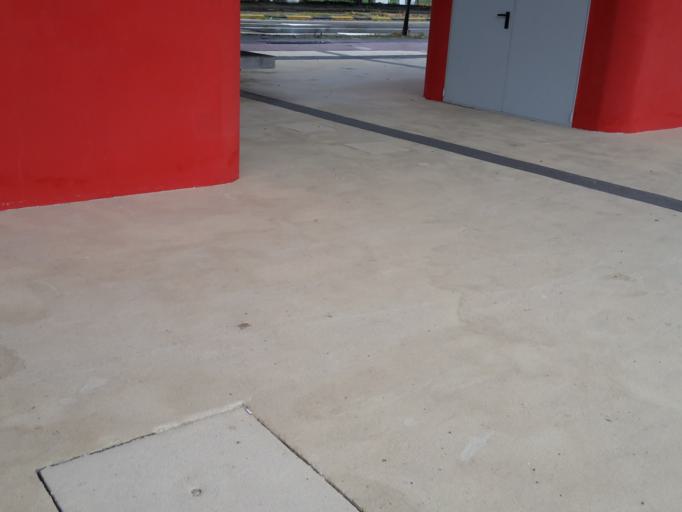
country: IT
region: Sardinia
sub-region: Provincia di Cagliari
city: Monserrato
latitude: 39.2695
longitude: 9.1265
